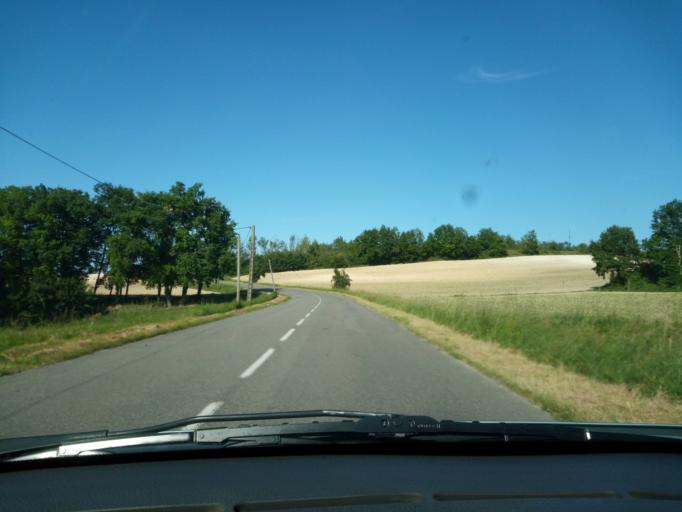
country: FR
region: Midi-Pyrenees
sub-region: Departement du Lot
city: Castelnau-Montratier
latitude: 44.2848
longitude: 1.3708
